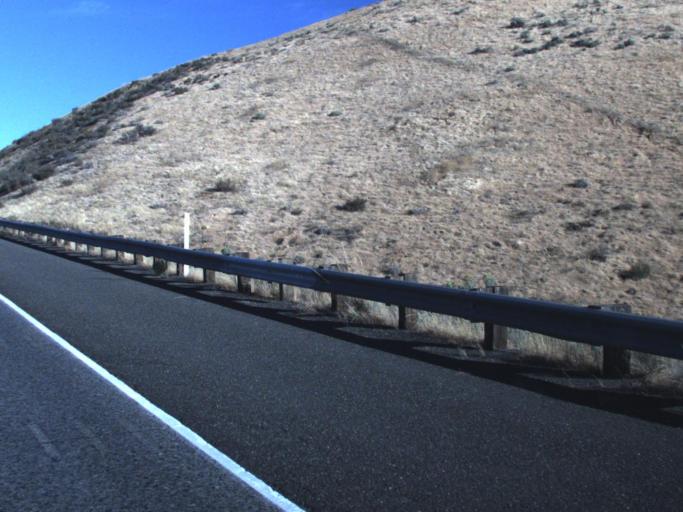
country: US
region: Washington
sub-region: Kittitas County
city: Kittitas
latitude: 46.8682
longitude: -120.4102
